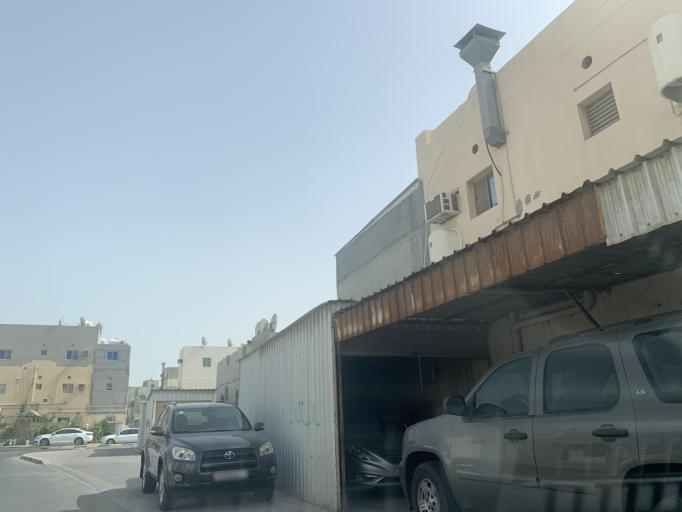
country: BH
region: Northern
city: Sitrah
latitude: 26.1708
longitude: 50.6227
